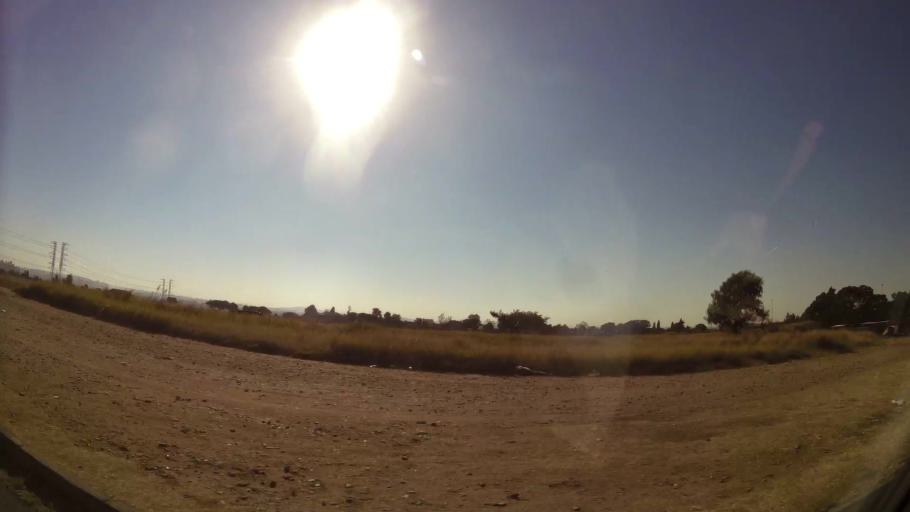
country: ZA
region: Gauteng
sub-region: Ekurhuleni Metropolitan Municipality
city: Germiston
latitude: -26.2458
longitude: 28.1046
